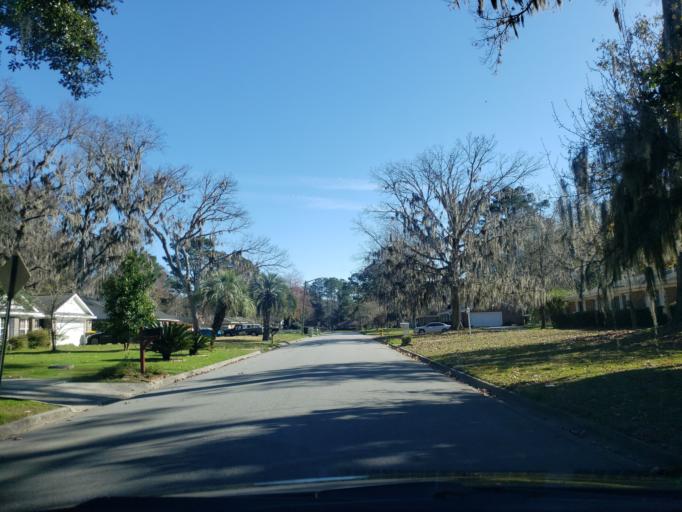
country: US
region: Georgia
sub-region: Chatham County
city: Montgomery
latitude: 31.9880
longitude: -81.1511
